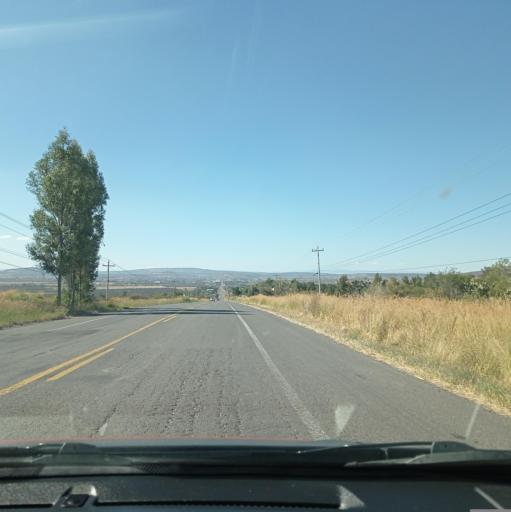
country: MX
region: Jalisco
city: San Miguel el Alto
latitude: 21.0156
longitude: -102.3272
